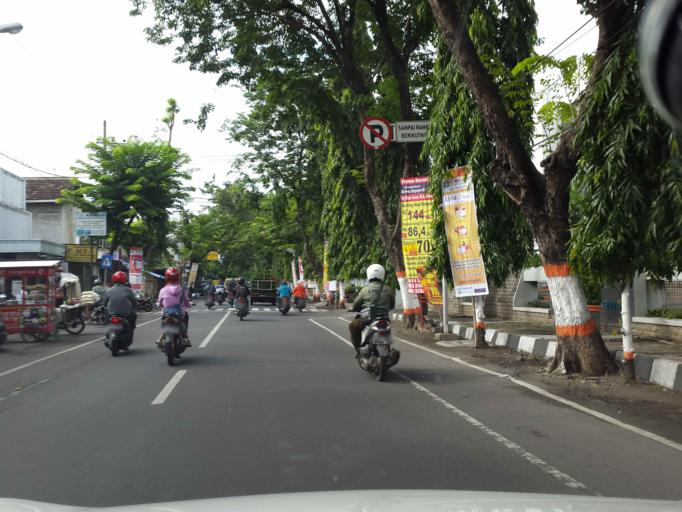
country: ID
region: East Java
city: Mojokerto
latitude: -7.4733
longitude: 112.4320
